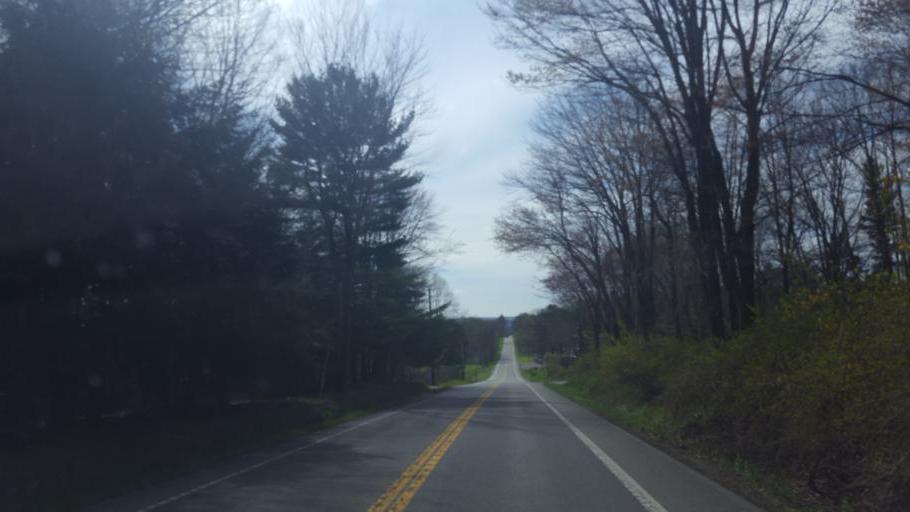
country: US
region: Pennsylvania
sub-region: Mercer County
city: Stoneboro
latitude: 41.3481
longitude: -80.0162
